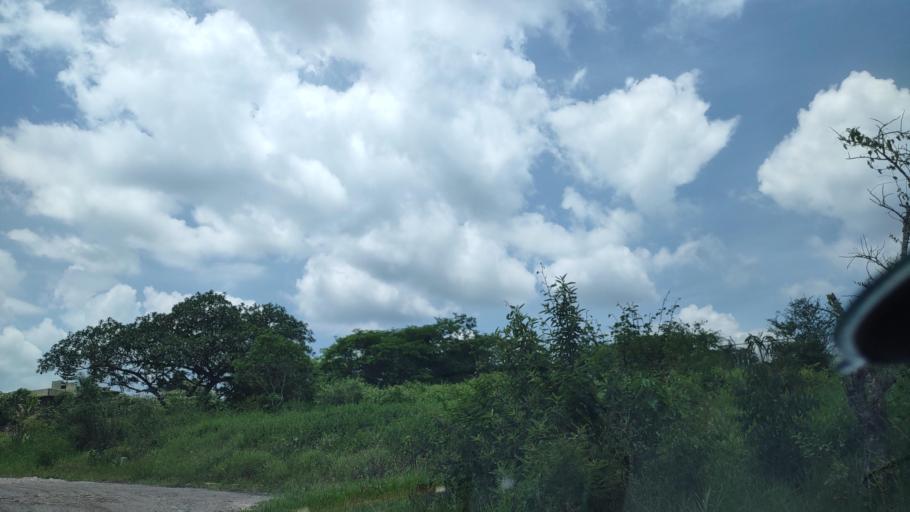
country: MX
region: Veracruz
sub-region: Emiliano Zapata
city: Dos Rios
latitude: 19.4653
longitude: -96.7920
